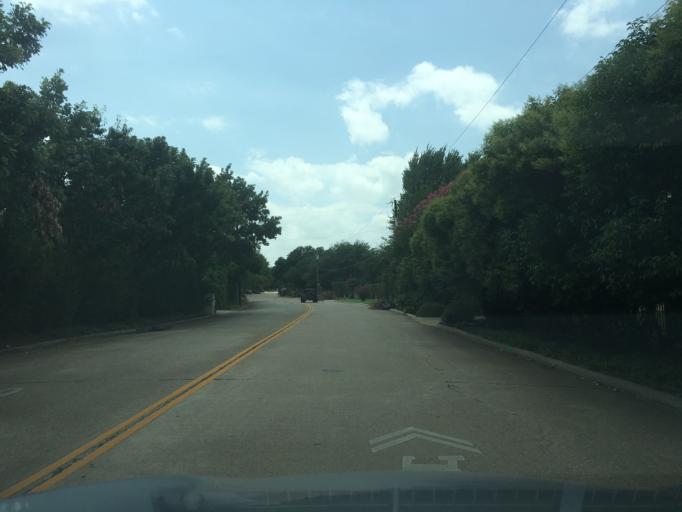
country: US
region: Texas
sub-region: Dallas County
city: University Park
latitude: 32.9023
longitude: -96.8250
